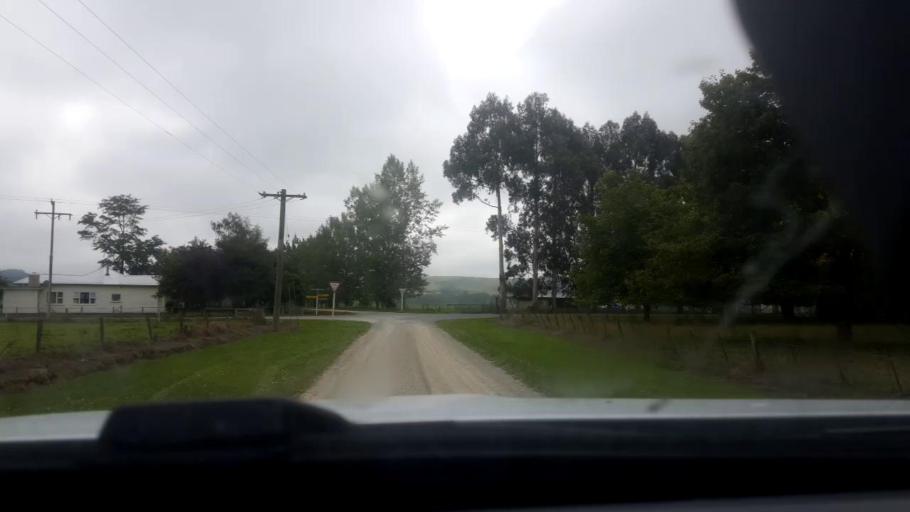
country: NZ
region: Canterbury
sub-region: Timaru District
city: Pleasant Point
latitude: -44.2075
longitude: 171.1132
